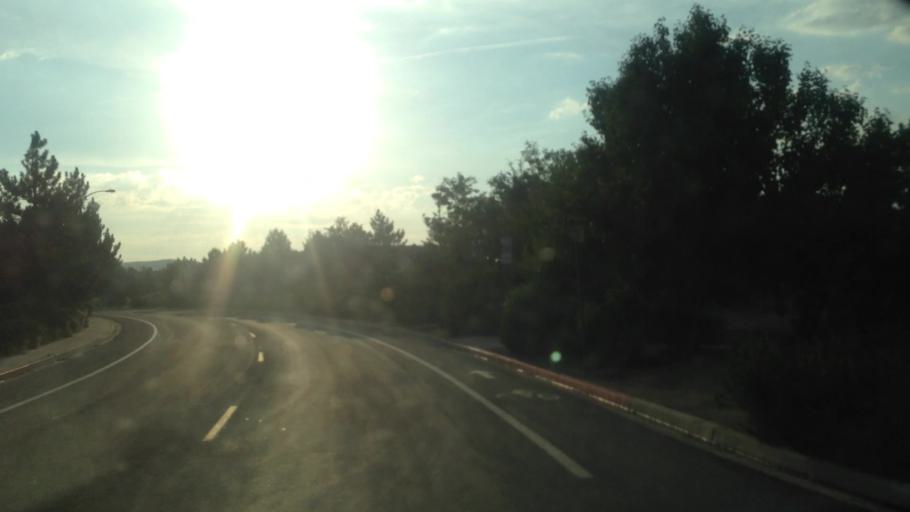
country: US
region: Nevada
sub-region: Washoe County
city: Lemmon Valley
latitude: 39.6258
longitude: -119.8736
